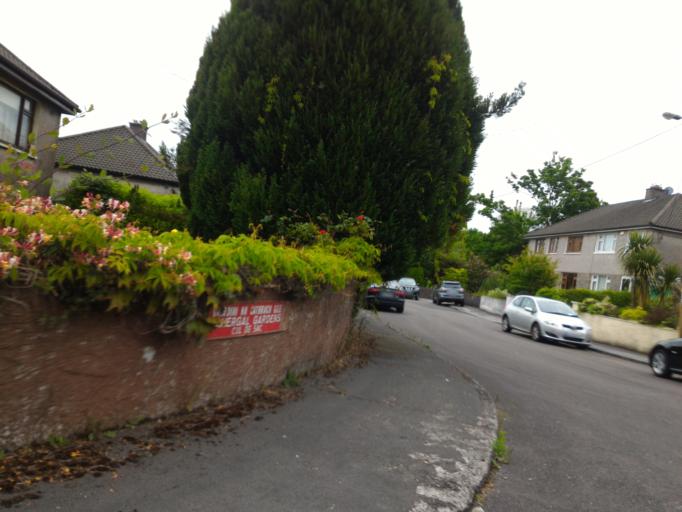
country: IE
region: Munster
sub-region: County Cork
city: Cork
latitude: 51.9120
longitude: -8.4522
